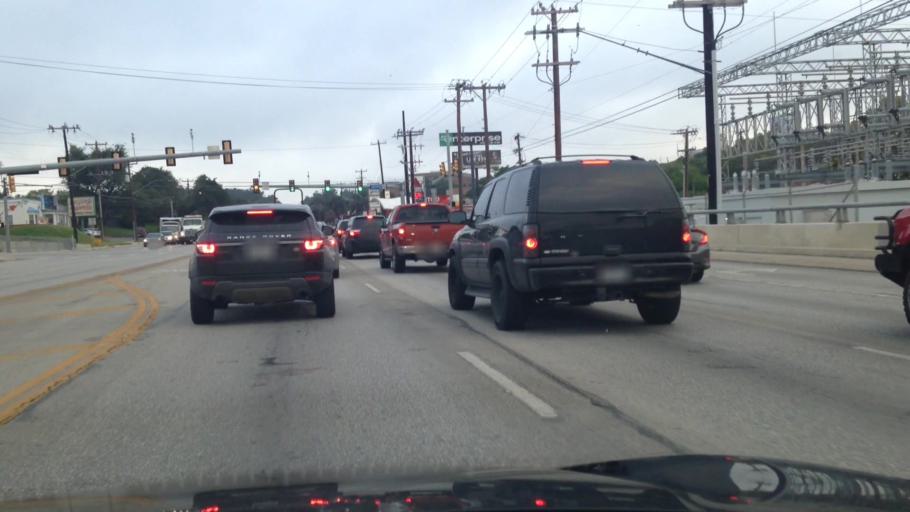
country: US
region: Texas
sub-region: Bexar County
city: Balcones Heights
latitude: 29.5024
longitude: -98.5599
